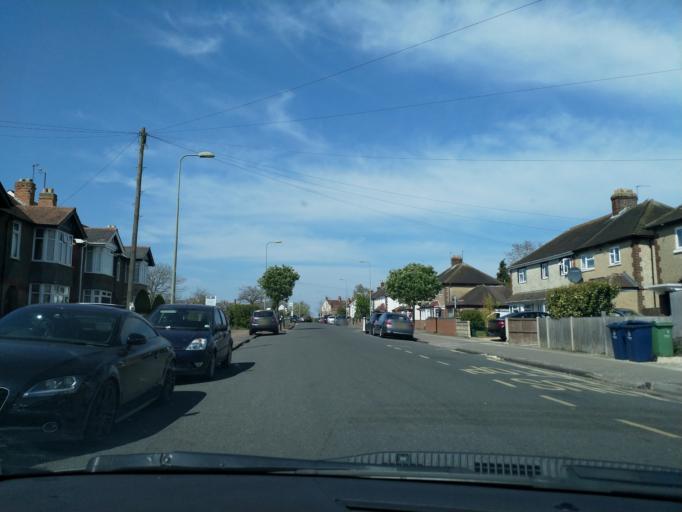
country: GB
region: England
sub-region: Oxfordshire
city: Cowley
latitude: 51.7386
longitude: -1.2034
